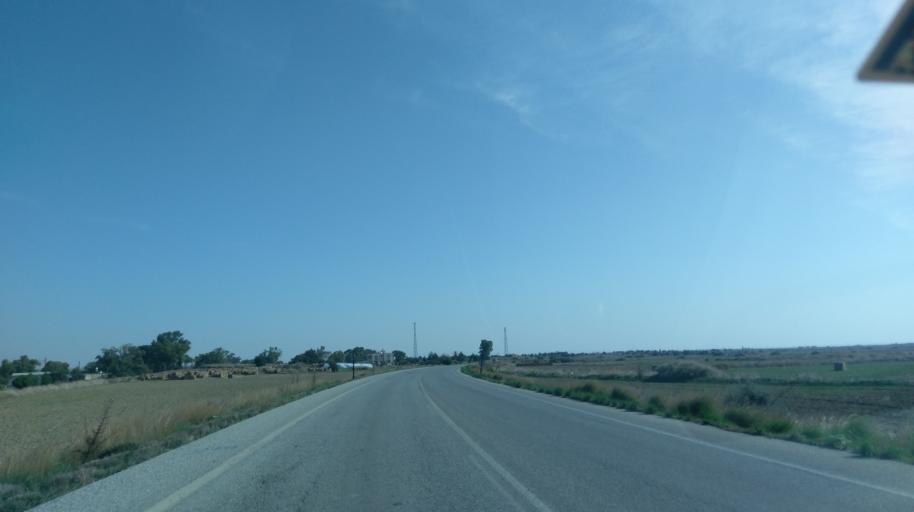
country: CY
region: Ammochostos
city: Lefkonoiko
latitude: 35.2600
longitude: 33.6532
